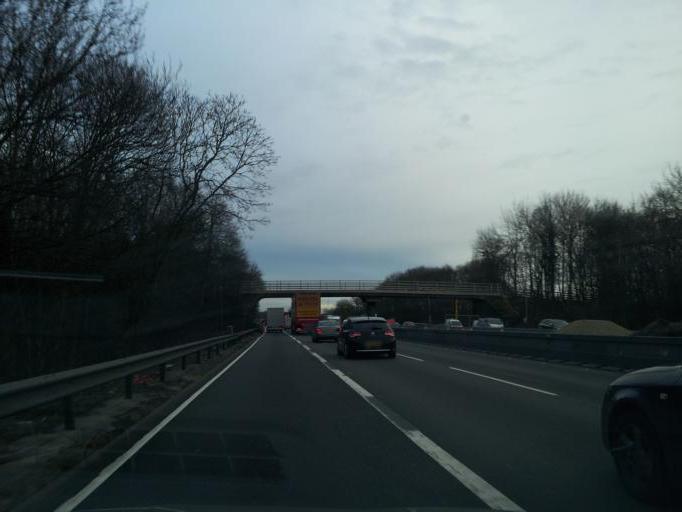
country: GB
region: England
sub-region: Northamptonshire
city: Long Buckby
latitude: 52.2598
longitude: -1.0847
